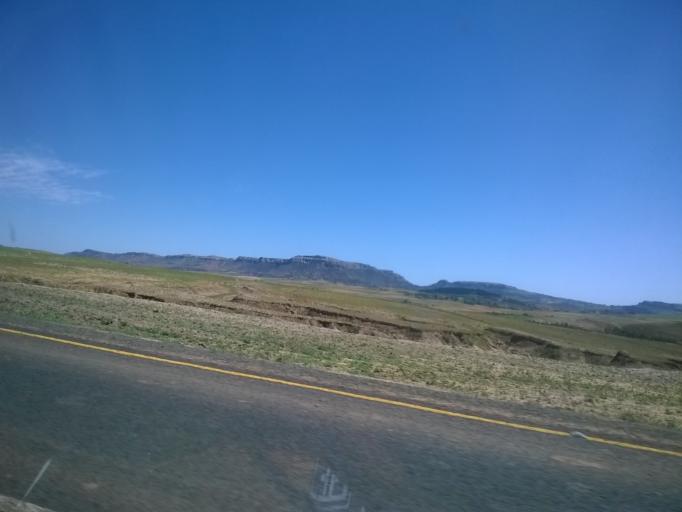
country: LS
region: Berea
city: Teyateyaneng
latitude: -29.0827
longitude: 27.9051
